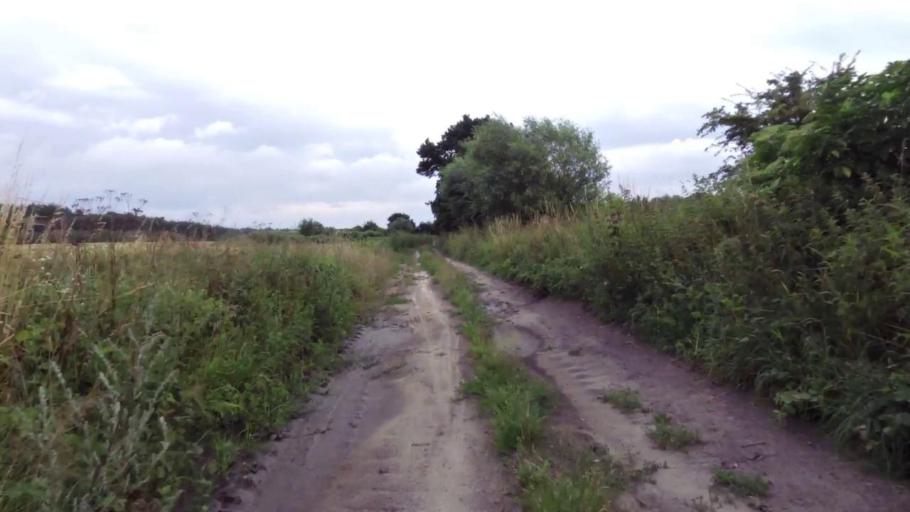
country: PL
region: West Pomeranian Voivodeship
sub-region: Powiat mysliborski
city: Mysliborz
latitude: 52.9635
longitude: 14.8994
